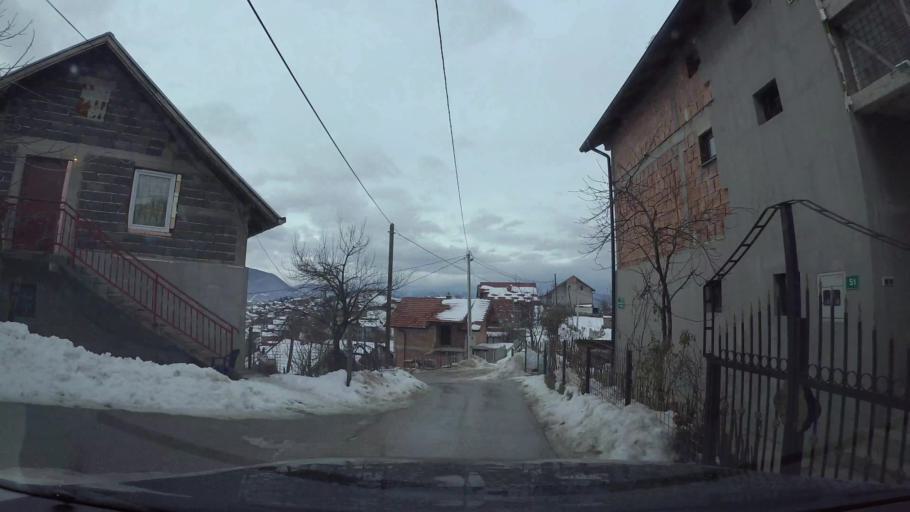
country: BA
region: Federation of Bosnia and Herzegovina
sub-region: Kanton Sarajevo
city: Sarajevo
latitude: 43.8643
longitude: 18.3516
